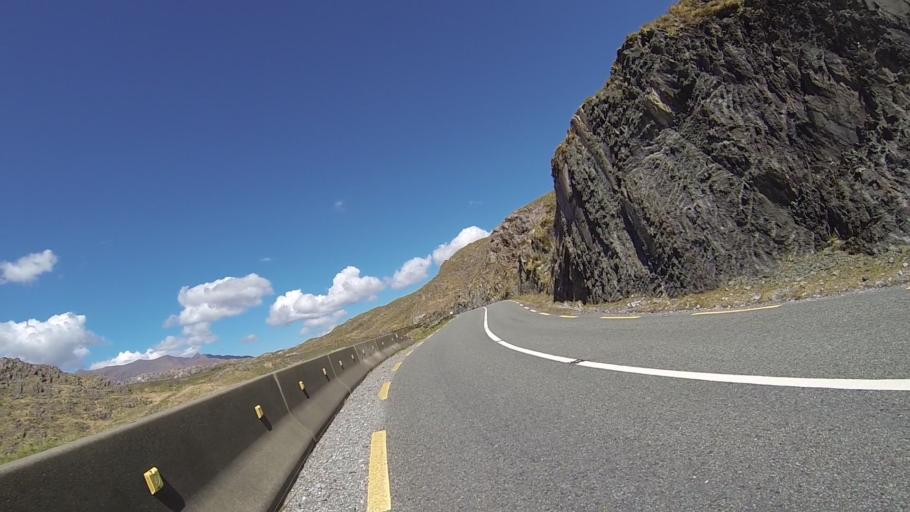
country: IE
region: Munster
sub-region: Ciarrai
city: Kenmare
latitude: 51.9344
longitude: -9.6530
